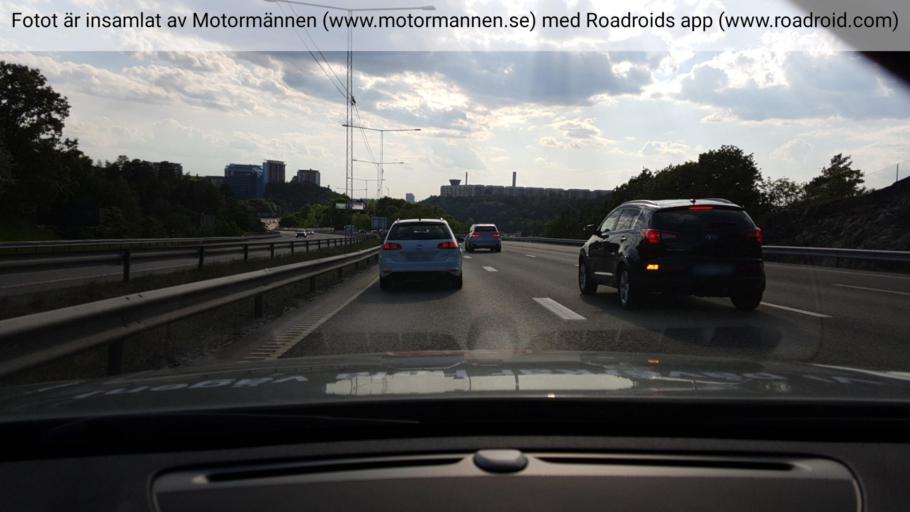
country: SE
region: Stockholm
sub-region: Nacka Kommun
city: Nacka
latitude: 59.3110
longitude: 18.1384
